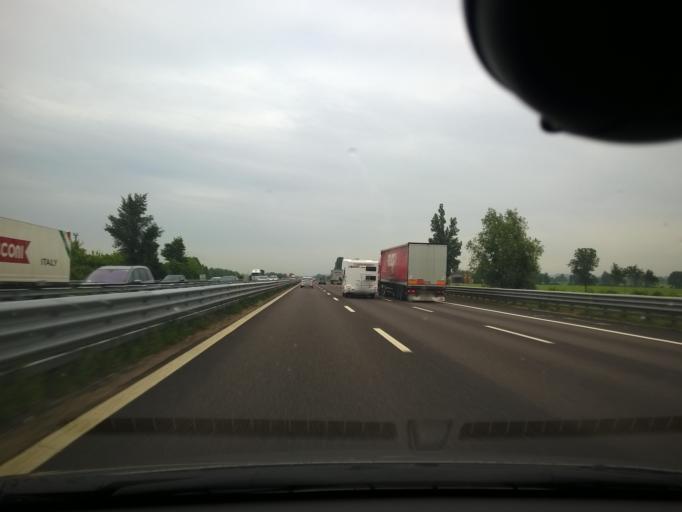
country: IT
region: Lombardy
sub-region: Provincia di Brescia
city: San Martino della Battaglia
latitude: 45.4396
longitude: 10.5712
